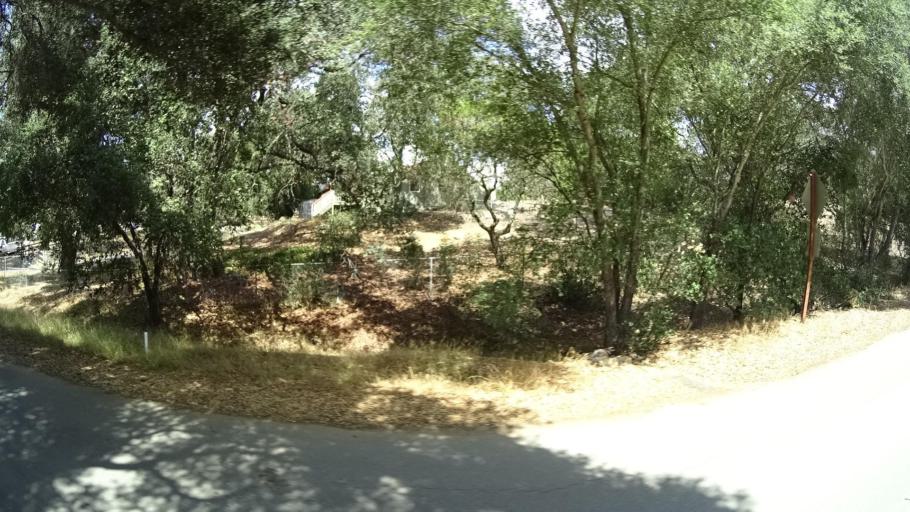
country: US
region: California
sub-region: San Diego County
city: Valley Center
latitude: 33.2014
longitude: -117.0365
